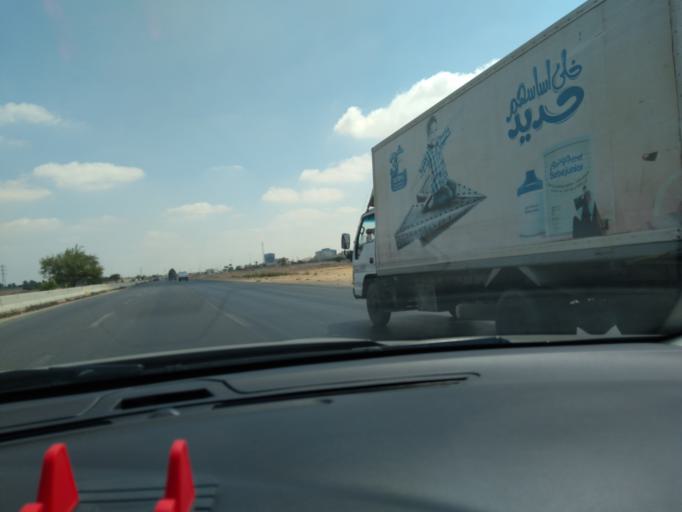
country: EG
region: Al Isma'iliyah
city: At Tall al Kabir
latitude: 30.3374
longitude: 31.8611
